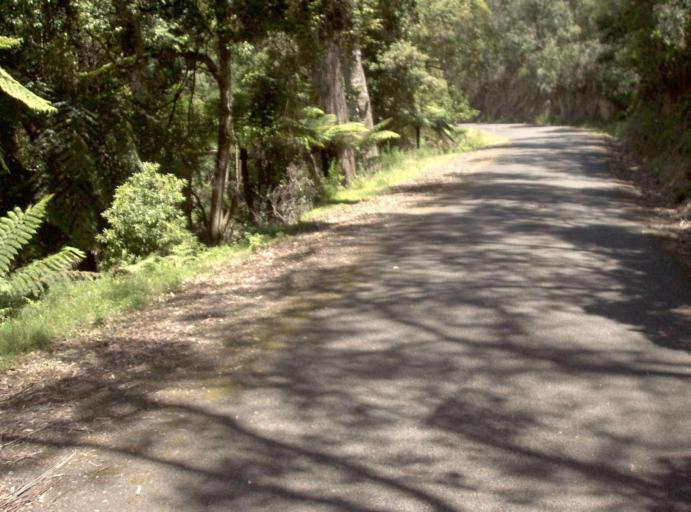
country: AU
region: New South Wales
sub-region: Bombala
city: Bombala
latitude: -37.4668
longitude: 148.9336
